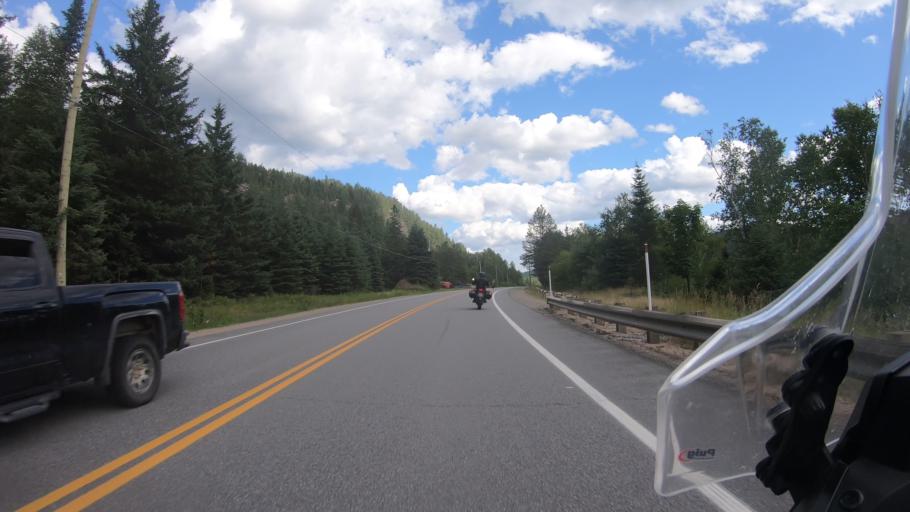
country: CA
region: Quebec
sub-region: Mauricie
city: Saint-Tite
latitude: 46.9932
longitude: -72.9158
